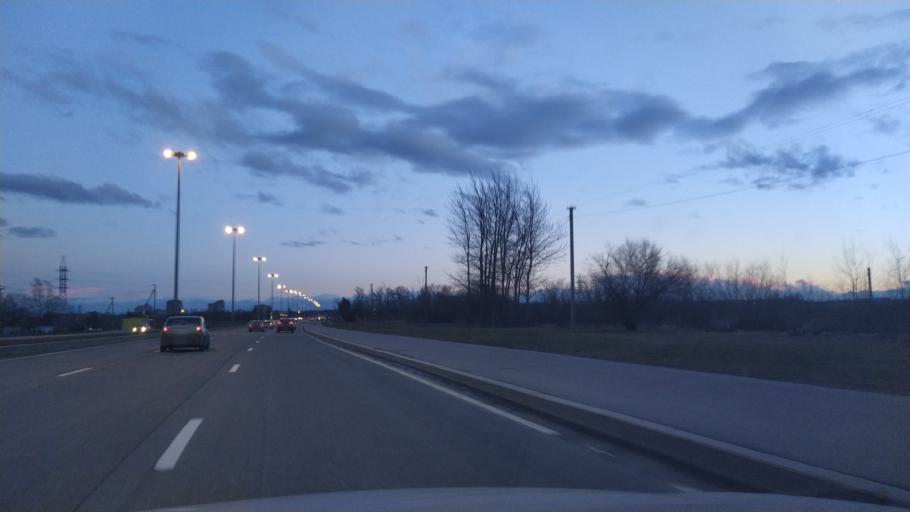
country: RU
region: St.-Petersburg
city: Pushkin
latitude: 59.7501
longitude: 30.3924
